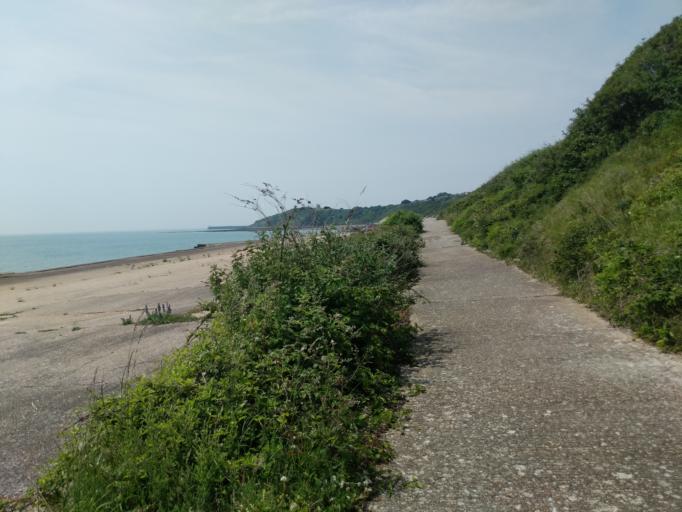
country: GB
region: England
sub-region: Kent
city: Folkestone
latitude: 51.0956
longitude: 1.2116
